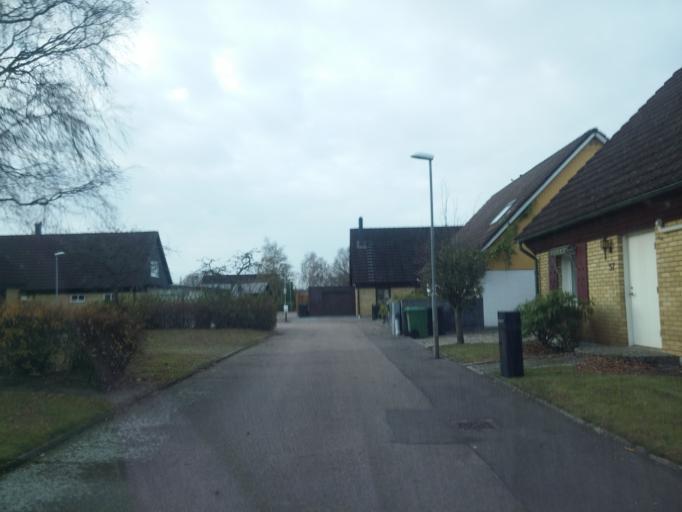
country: SE
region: Skane
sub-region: Angelholms Kommun
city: AEngelholm
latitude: 56.2314
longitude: 12.8402
